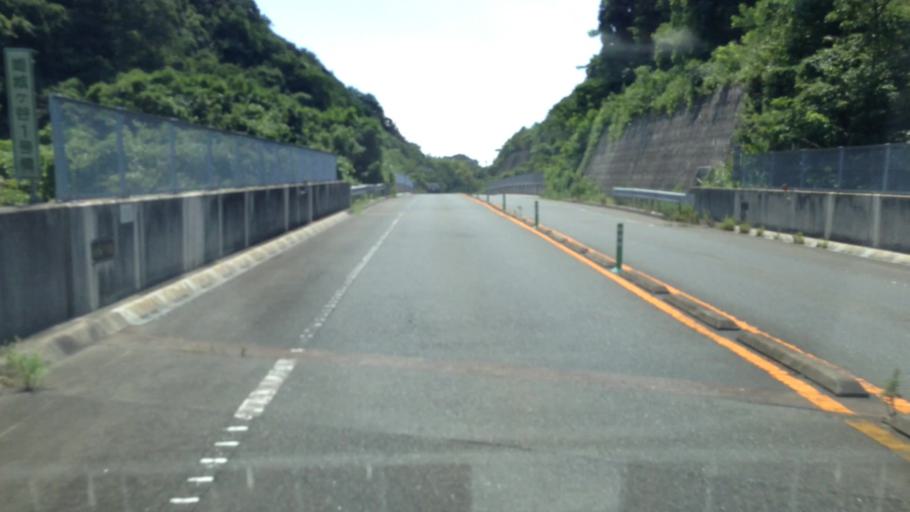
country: JP
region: Kanagawa
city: Yokosuka
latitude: 35.2360
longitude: 139.6512
